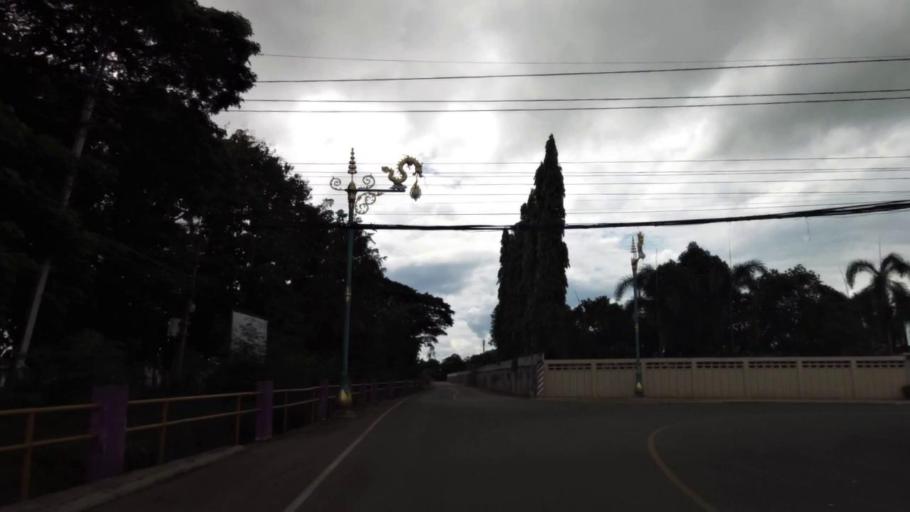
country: TH
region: Nakhon Sawan
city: Phai Sali
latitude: 15.5971
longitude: 100.6538
